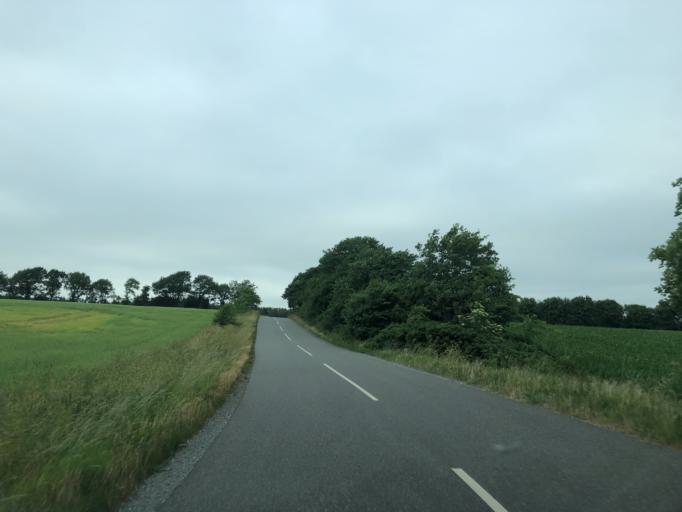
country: DK
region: Central Jutland
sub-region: Holstebro Kommune
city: Holstebro
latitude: 56.2573
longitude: 8.6321
